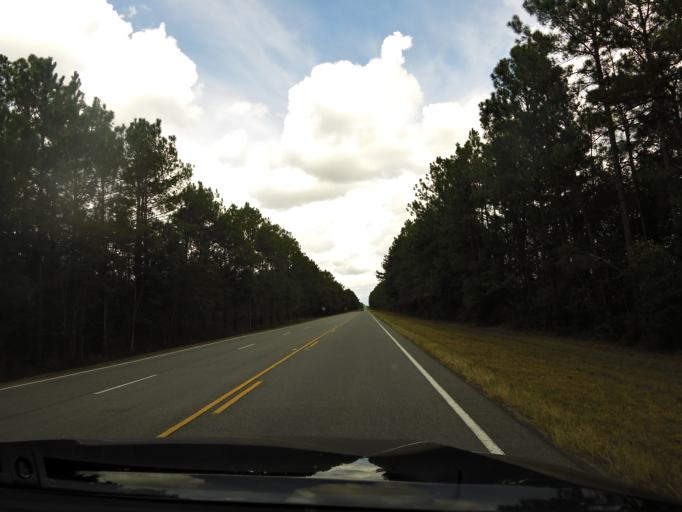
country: US
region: Georgia
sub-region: Brantley County
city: Nahunta
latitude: 31.0224
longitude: -82.0236
